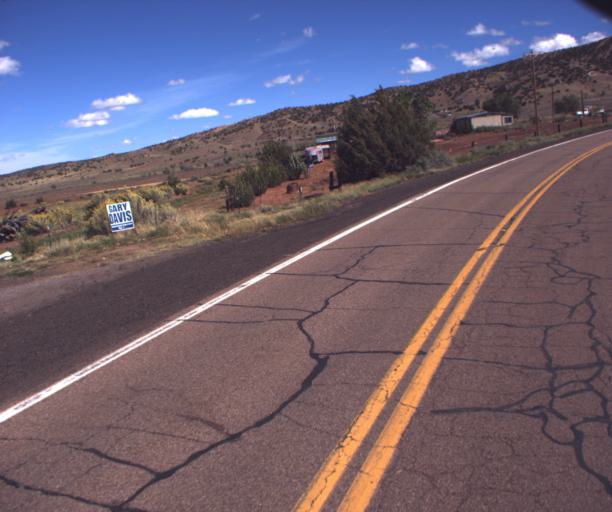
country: US
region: Arizona
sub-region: Apache County
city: Saint Johns
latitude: 34.4781
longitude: -109.6046
